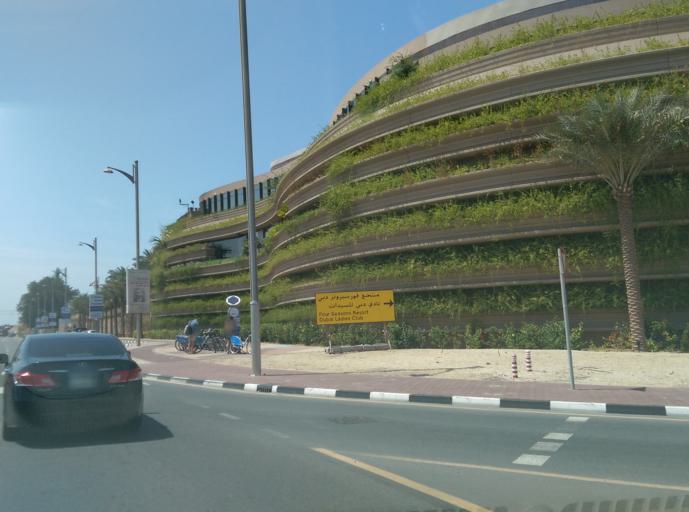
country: AE
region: Dubai
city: Dubai
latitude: 25.2028
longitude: 55.2411
